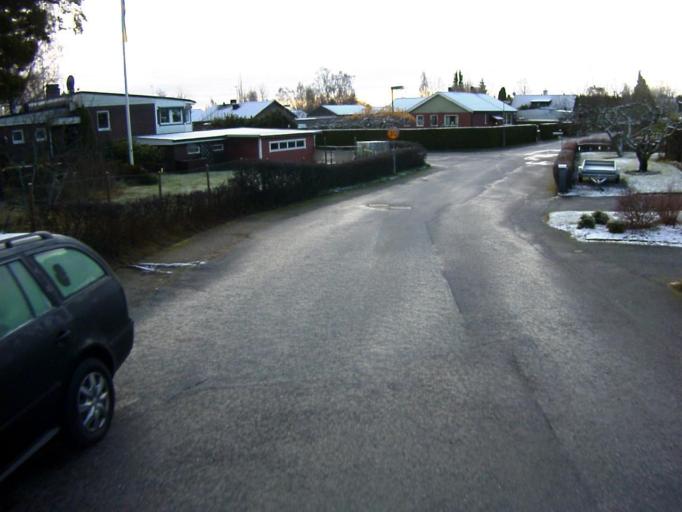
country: SE
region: Soedermanland
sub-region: Eskilstuna Kommun
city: Hallbybrunn
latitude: 59.3941
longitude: 16.4119
